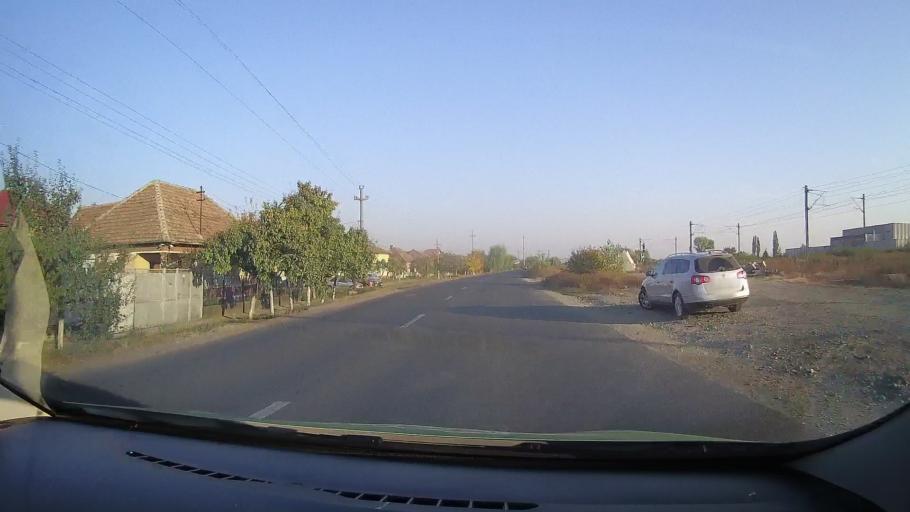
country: RO
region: Arad
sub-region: Comuna Sofronea
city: Sofronea
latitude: 46.2790
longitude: 21.3138
